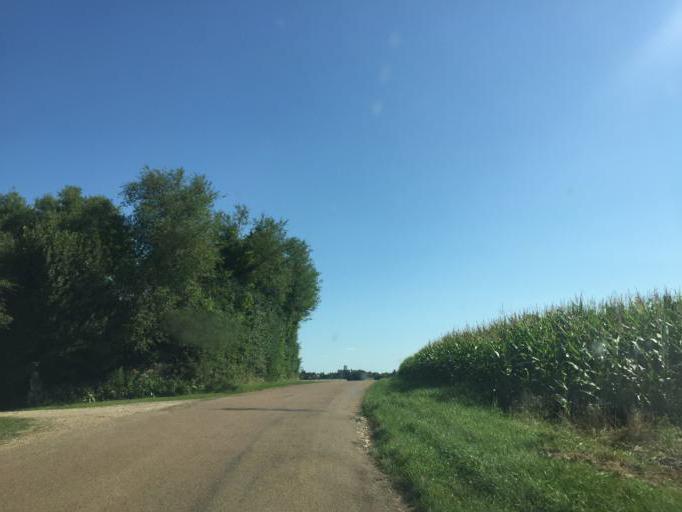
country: FR
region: Bourgogne
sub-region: Departement de l'Yonne
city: Fontenailles
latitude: 47.5186
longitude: 3.3464
